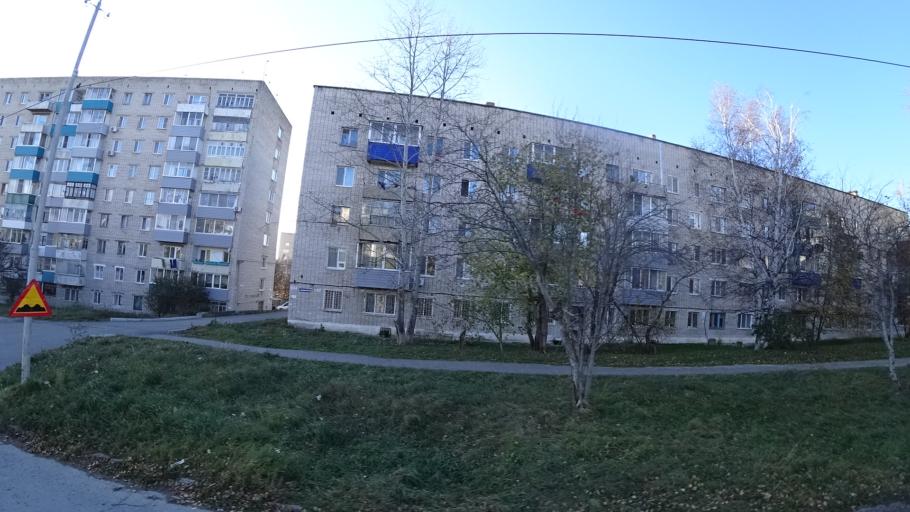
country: RU
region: Khabarovsk Krai
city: Amursk
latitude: 50.2283
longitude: 136.9110
